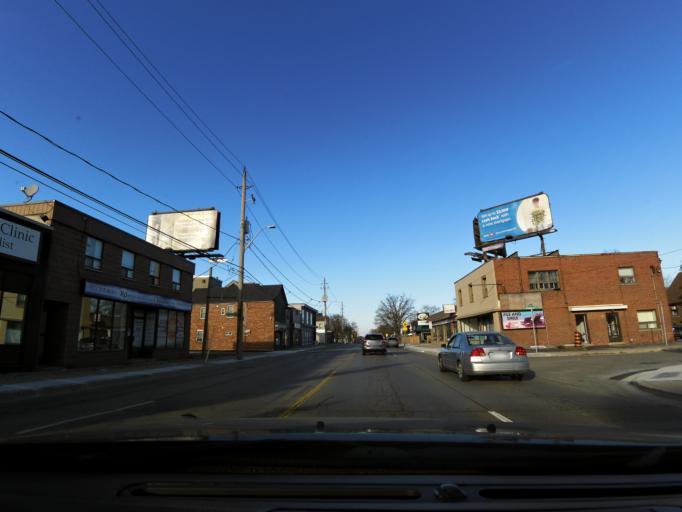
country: CA
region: Ontario
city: Hamilton
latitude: 43.2405
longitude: -79.8766
